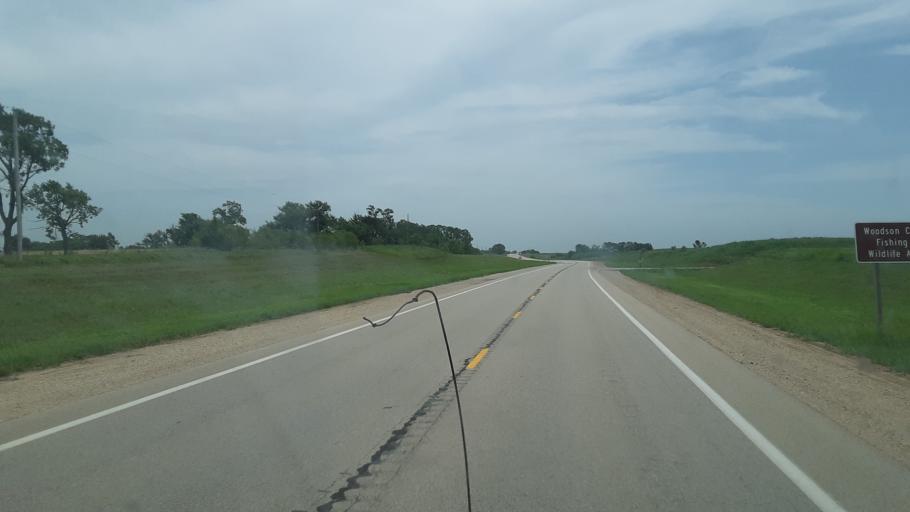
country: US
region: Kansas
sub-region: Woodson County
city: Yates Center
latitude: 37.8362
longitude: -95.8726
